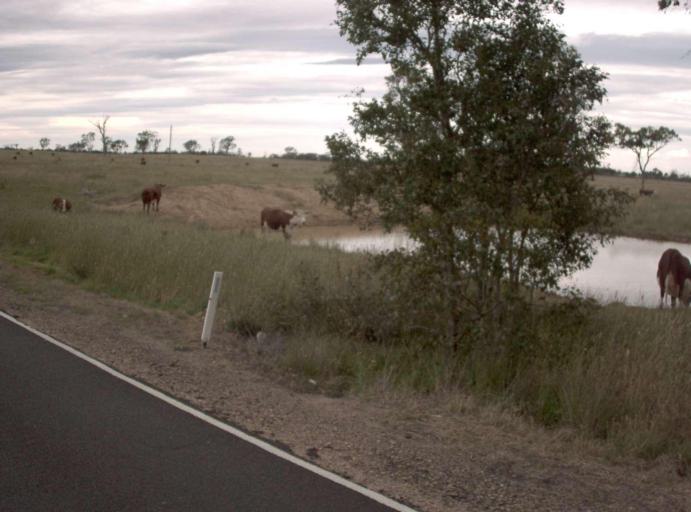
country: AU
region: Victoria
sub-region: Wellington
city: Sale
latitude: -38.0018
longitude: 147.1910
